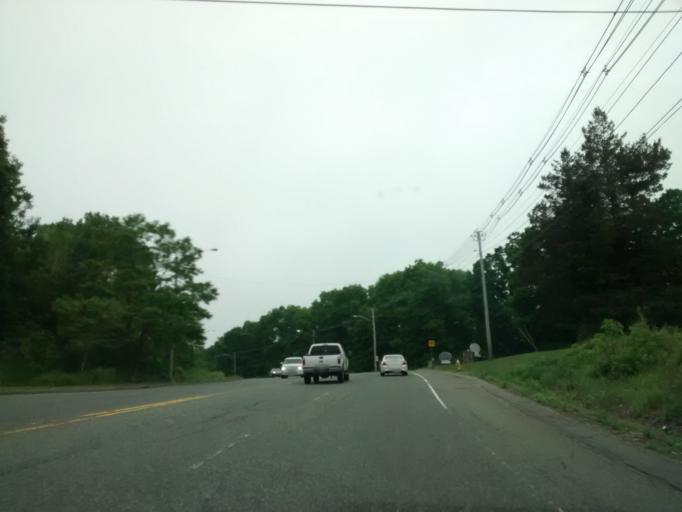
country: US
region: Massachusetts
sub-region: Worcester County
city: Hamilton
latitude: 42.2890
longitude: -71.7612
